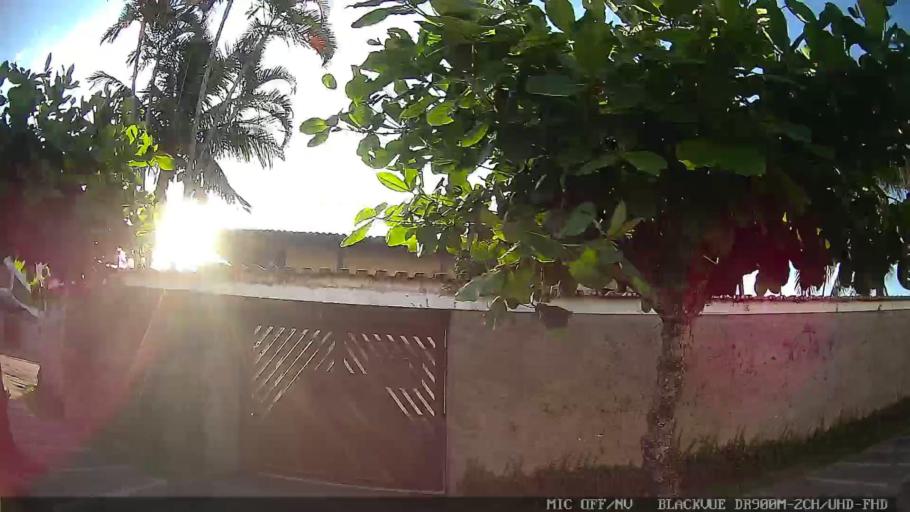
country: BR
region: Sao Paulo
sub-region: Peruibe
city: Peruibe
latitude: -24.2963
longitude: -46.9663
